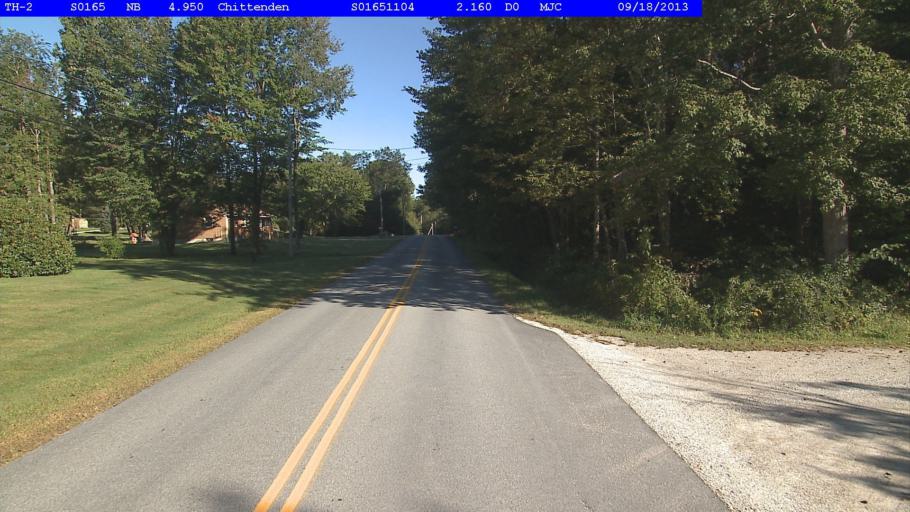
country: US
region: Vermont
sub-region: Rutland County
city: Rutland
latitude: 43.7068
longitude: -72.9612
